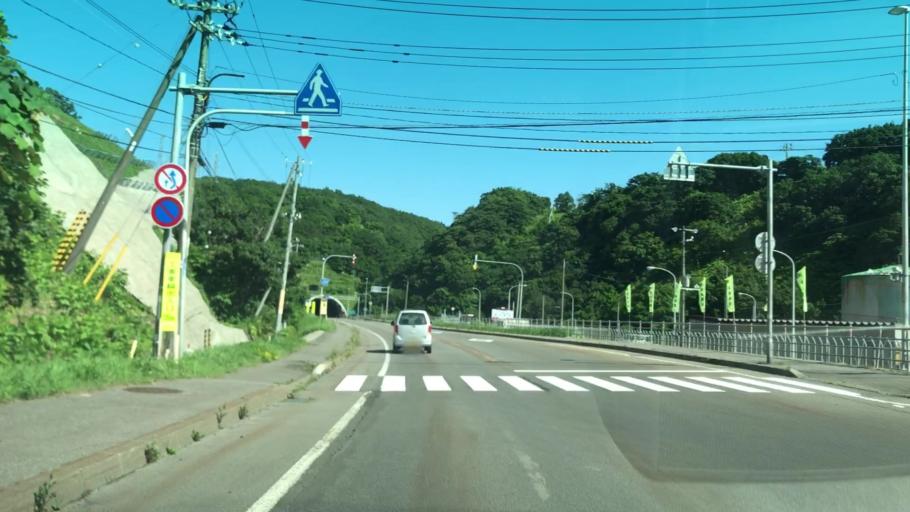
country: JP
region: Hokkaido
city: Iwanai
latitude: 43.0425
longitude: 140.5092
